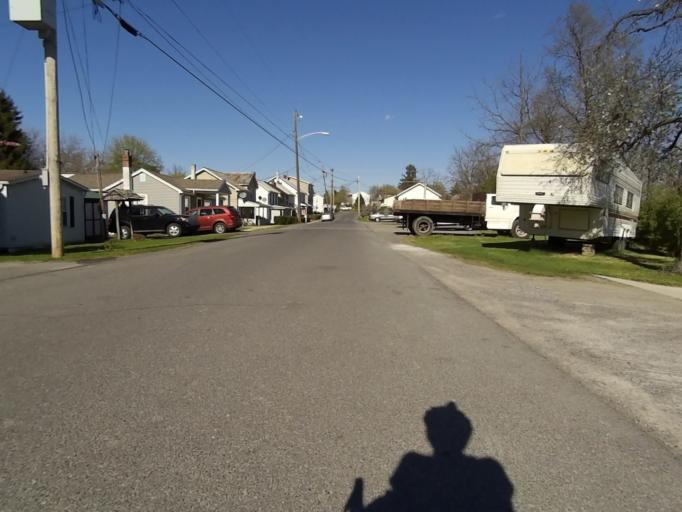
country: US
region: Pennsylvania
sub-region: Centre County
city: Bellefonte
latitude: 40.9078
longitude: -77.7916
